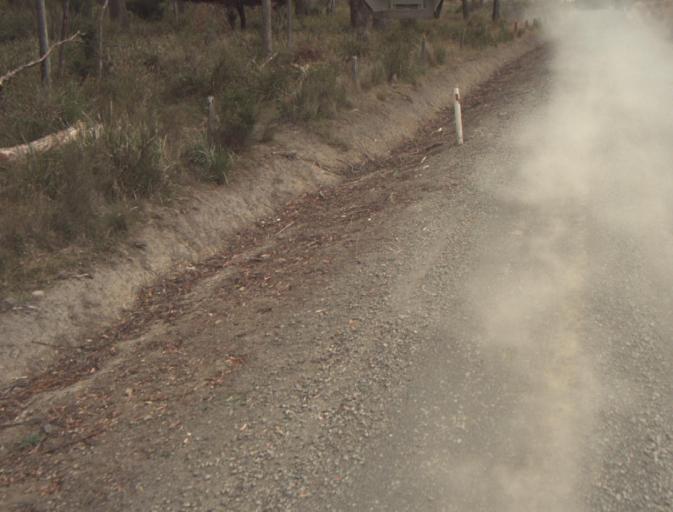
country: AU
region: Tasmania
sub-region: Northern Midlands
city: Evandale
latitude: -41.4649
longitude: 147.4485
